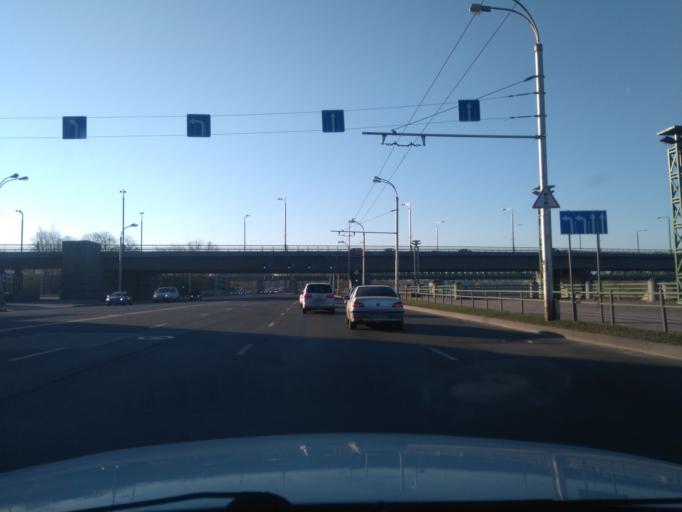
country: LT
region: Kauno apskritis
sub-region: Kaunas
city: Aleksotas
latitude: 54.8845
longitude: 23.9243
